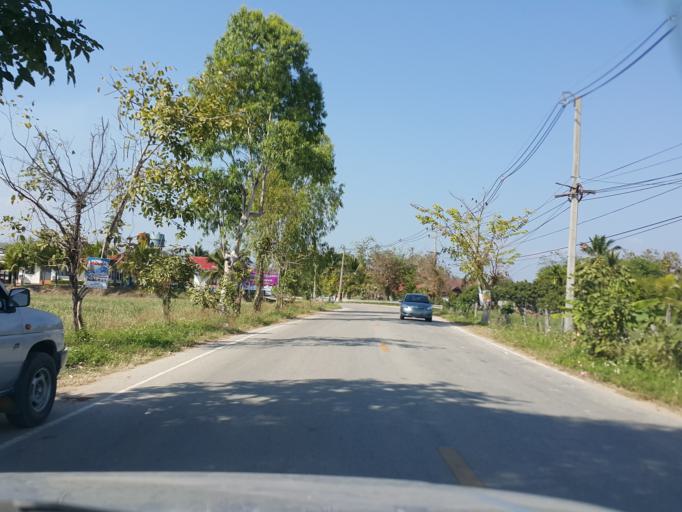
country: TH
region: Chiang Mai
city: Mae Wang
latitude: 18.6028
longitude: 98.7991
